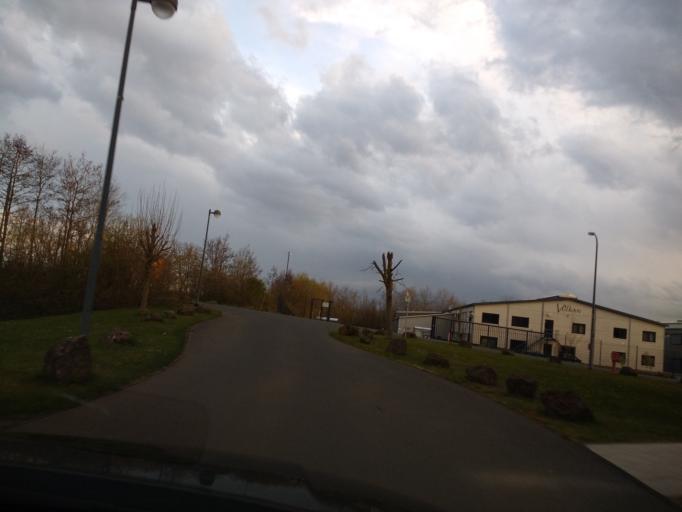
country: DE
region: Rheinland-Pfalz
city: Wiesbaum
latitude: 50.3478
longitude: 6.6735
